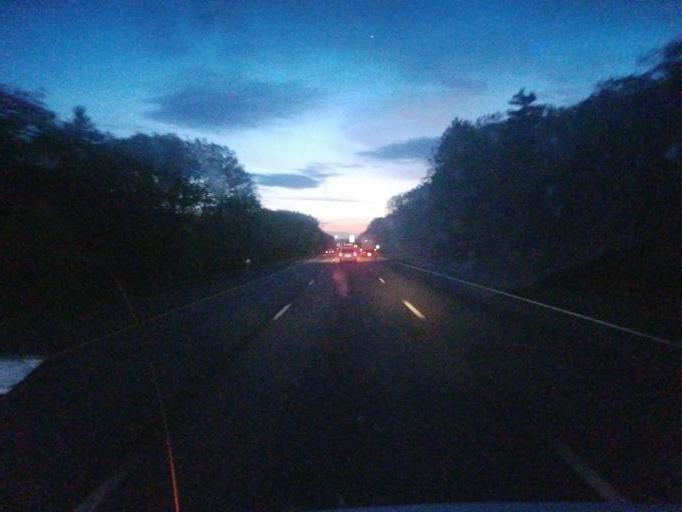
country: US
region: Massachusetts
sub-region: Worcester County
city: Bolton
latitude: 42.4226
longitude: -71.5994
